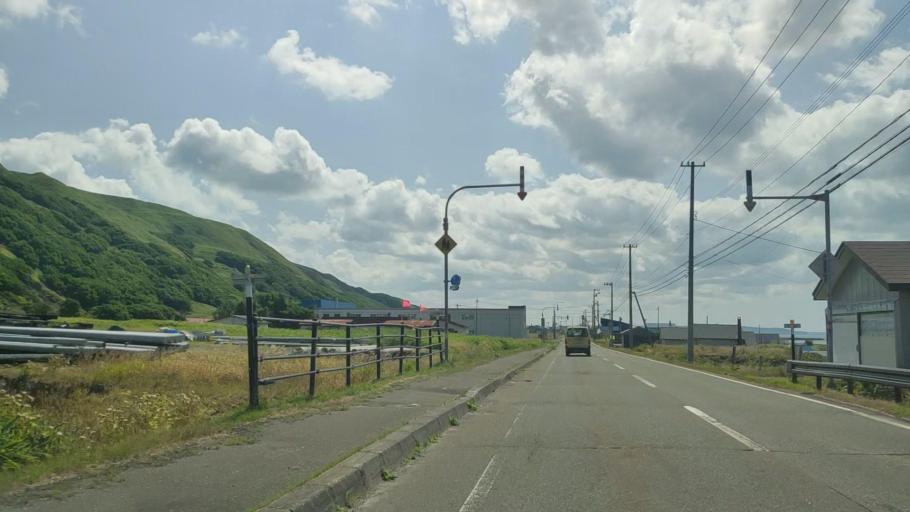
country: JP
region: Hokkaido
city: Wakkanai
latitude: 45.3987
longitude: 141.6376
